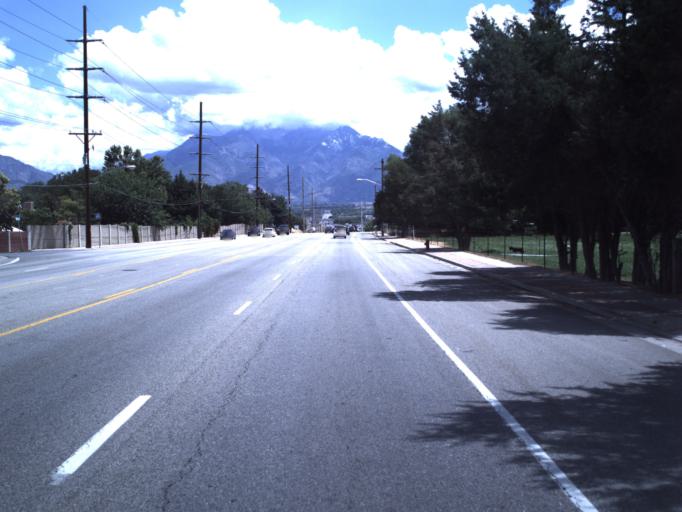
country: US
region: Utah
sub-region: Salt Lake County
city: West Jordan
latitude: 40.5877
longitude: -111.9261
